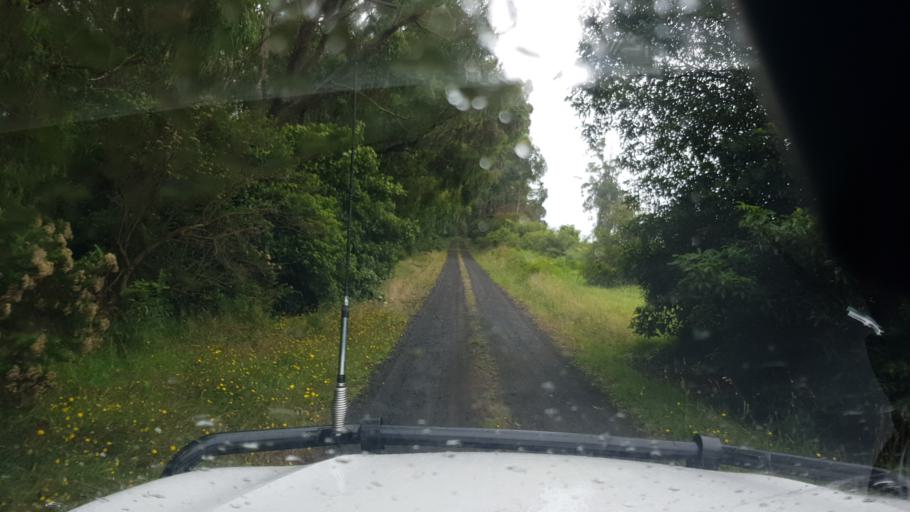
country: AU
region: Victoria
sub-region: Baw Baw
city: Warragul
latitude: -38.0881
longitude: 145.8911
